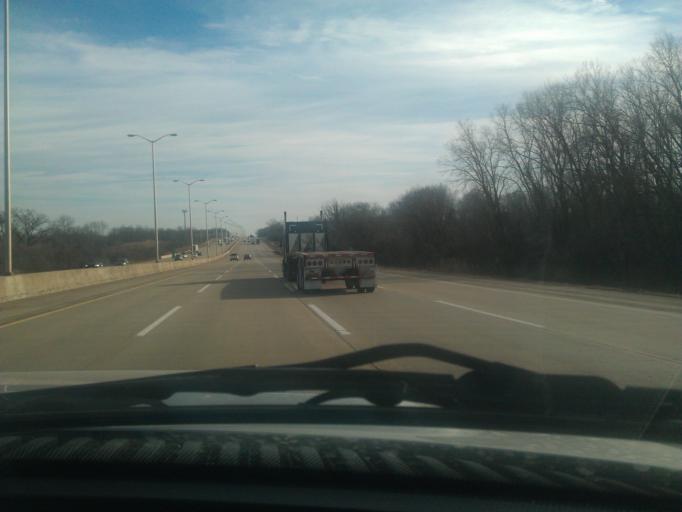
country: US
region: Illinois
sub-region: Lake County
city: Wadsworth
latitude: 42.4208
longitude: -87.9477
